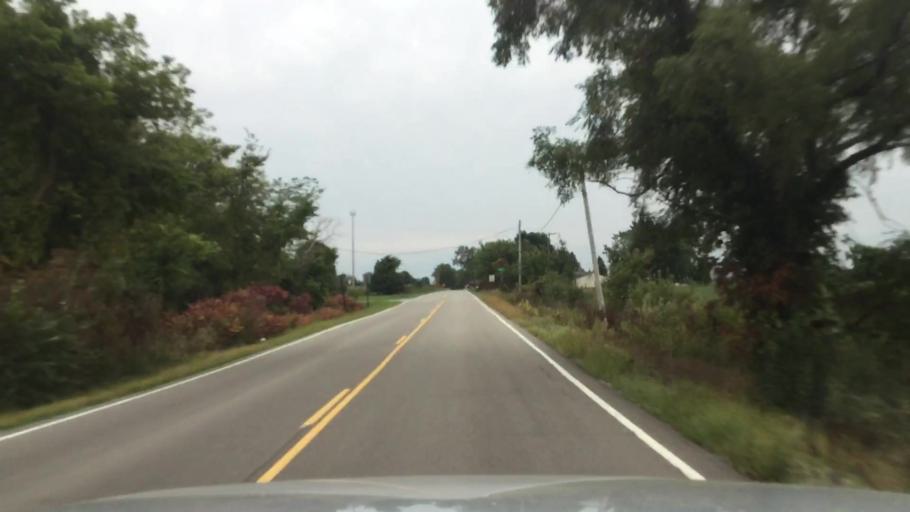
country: US
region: Michigan
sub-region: Washtenaw County
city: Milan
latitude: 42.0912
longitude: -83.7353
